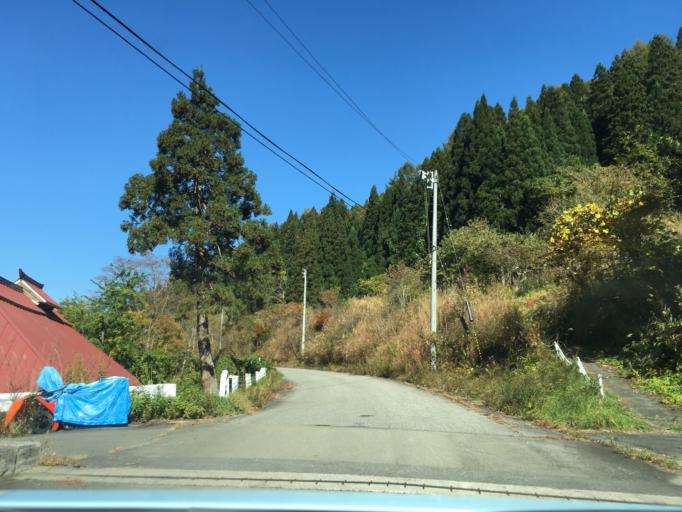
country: JP
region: Fukushima
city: Inawashiro
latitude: 37.4135
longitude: 139.9918
